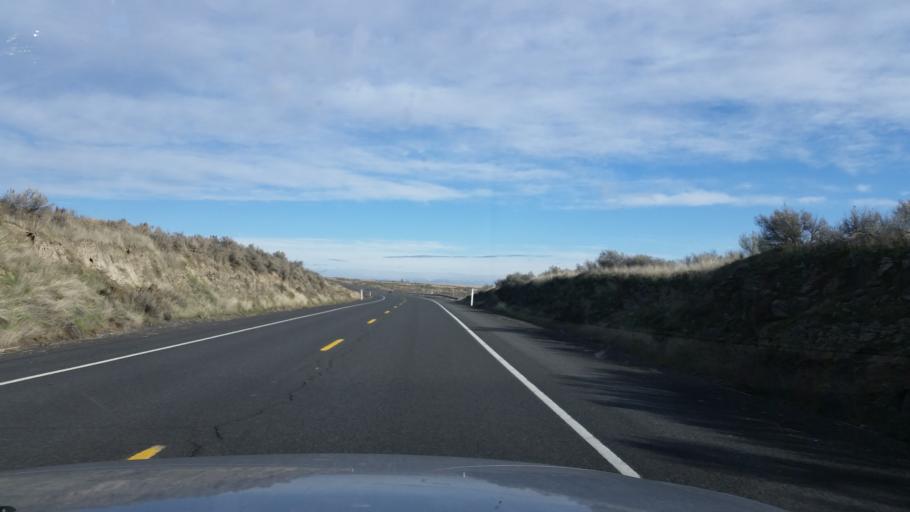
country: US
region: Washington
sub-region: Adams County
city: Ritzville
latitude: 47.3672
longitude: -118.4576
